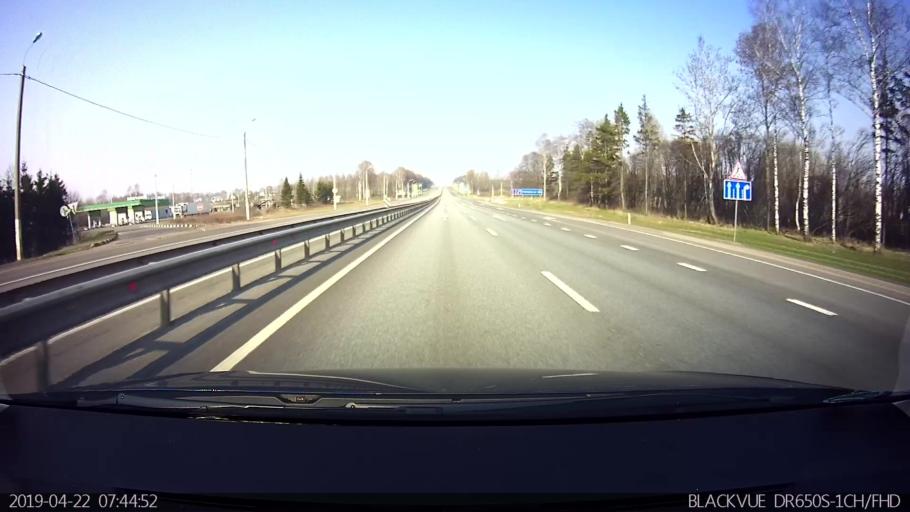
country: RU
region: Smolensk
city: Verkhnedneprovskiy
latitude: 55.1825
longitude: 33.5208
